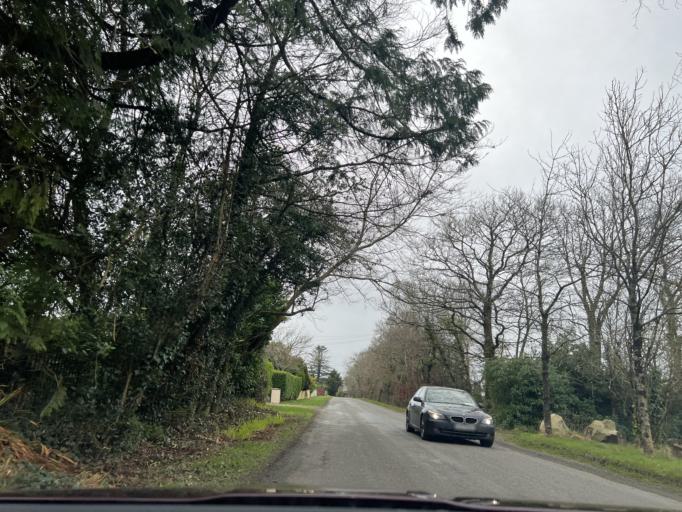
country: IE
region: Leinster
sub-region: Loch Garman
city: Castlebridge
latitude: 52.3836
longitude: -6.5250
